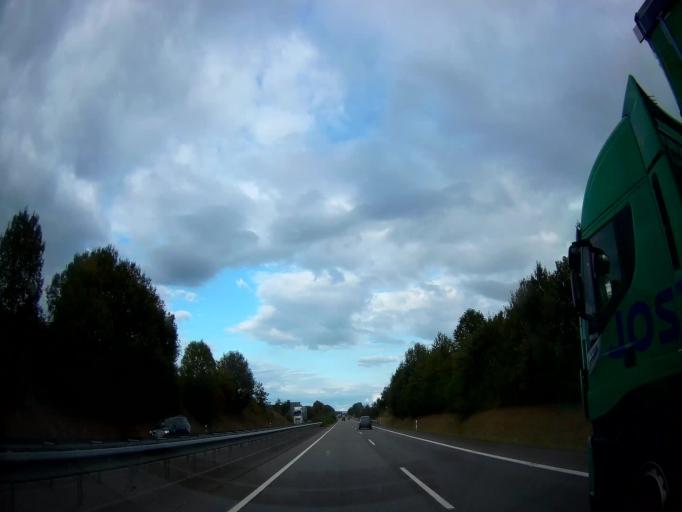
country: DE
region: Rheinland-Pfalz
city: Orsfeld
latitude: 50.0183
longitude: 6.6165
